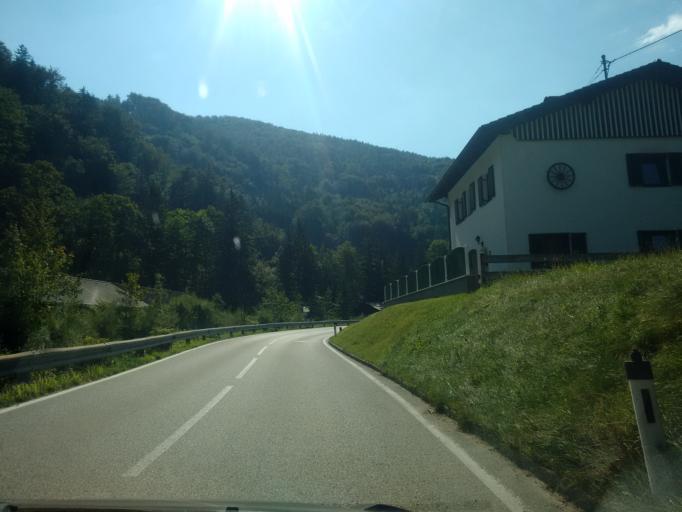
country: AT
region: Upper Austria
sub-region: Politischer Bezirk Gmunden
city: Gruenau im Almtal
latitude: 47.8456
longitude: 13.9498
